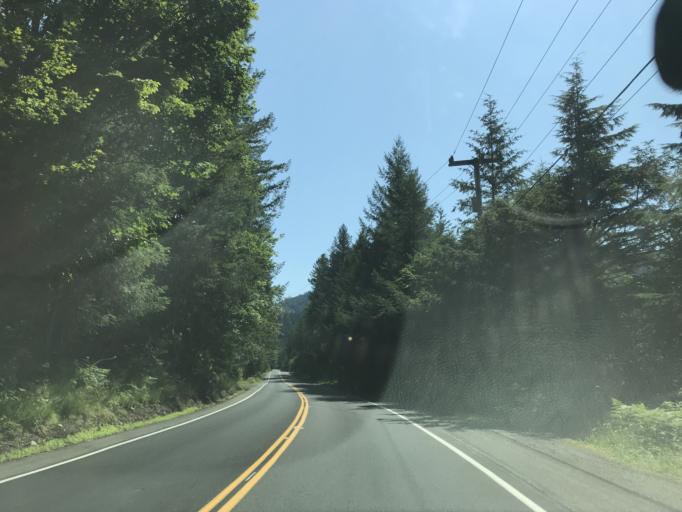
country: US
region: Washington
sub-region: King County
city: Ravensdale
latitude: 47.3563
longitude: -121.8987
